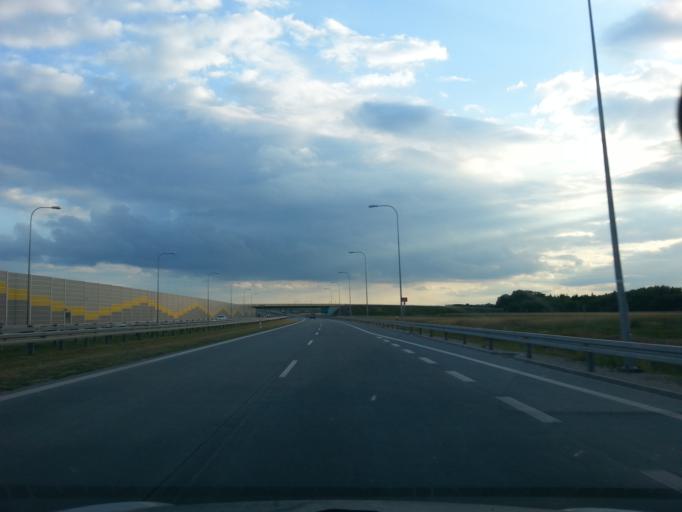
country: PL
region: Lodz Voivodeship
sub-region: Powiat zdunskowolski
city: Zapolice
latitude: 51.5915
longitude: 18.8174
